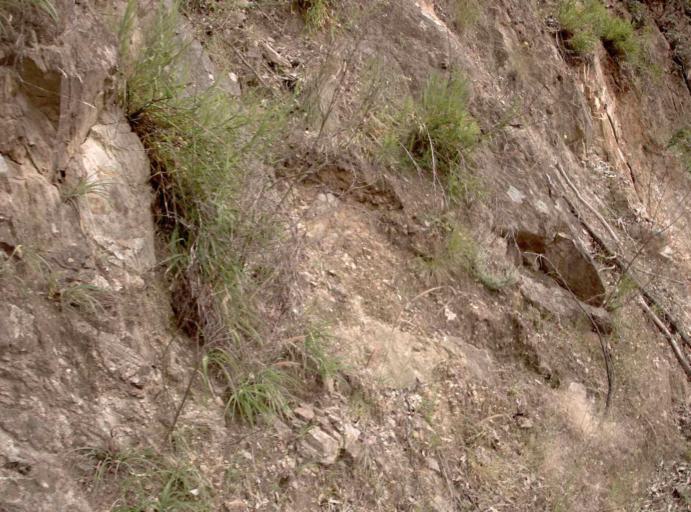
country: AU
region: Victoria
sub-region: Wellington
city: Heyfield
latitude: -37.7263
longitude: 146.6673
